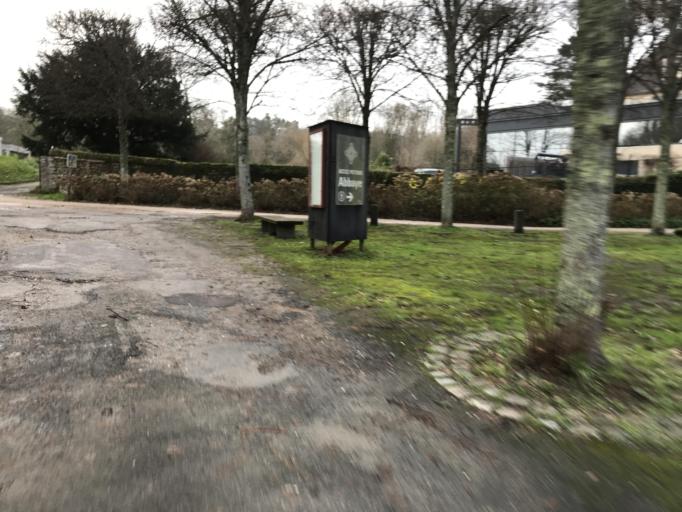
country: FR
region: Brittany
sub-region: Departement du Finistere
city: Daoulas
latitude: 48.3614
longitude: -4.2663
